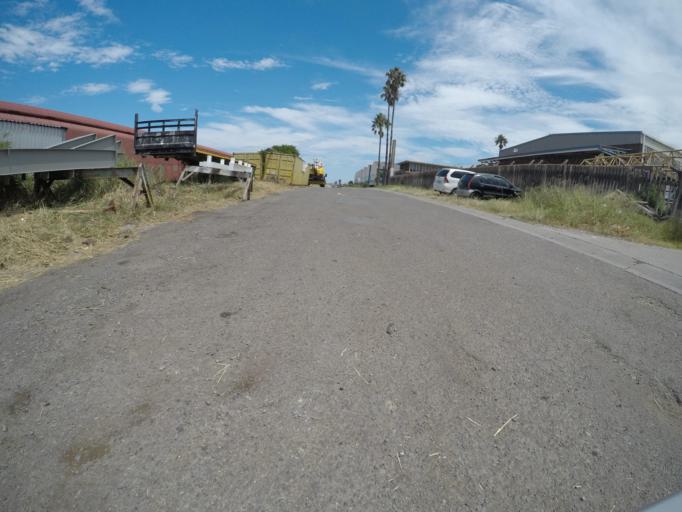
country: ZA
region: Eastern Cape
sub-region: Buffalo City Metropolitan Municipality
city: East London
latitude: -33.0289
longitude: 27.8790
